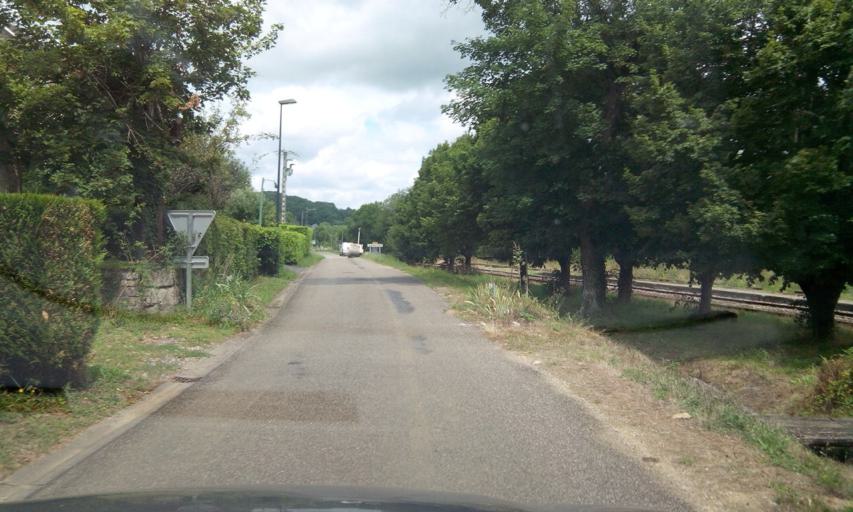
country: FR
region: Limousin
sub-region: Departement de la Correze
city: Meyssac
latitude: 45.0386
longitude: 1.6001
